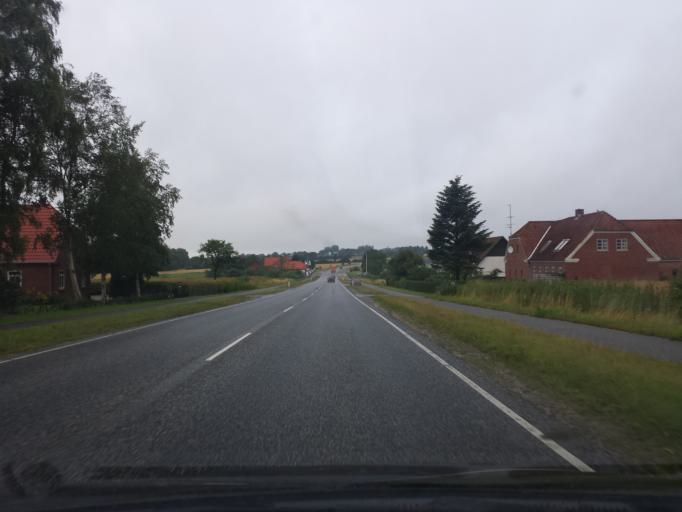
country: DK
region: South Denmark
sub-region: Sonderborg Kommune
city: Guderup
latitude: 54.9747
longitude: 9.8905
